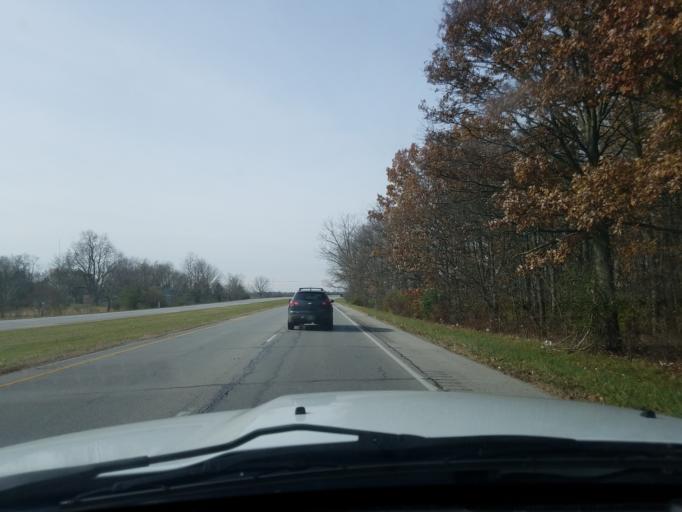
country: US
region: Indiana
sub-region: Delaware County
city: Yorktown
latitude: 40.2166
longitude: -85.4503
